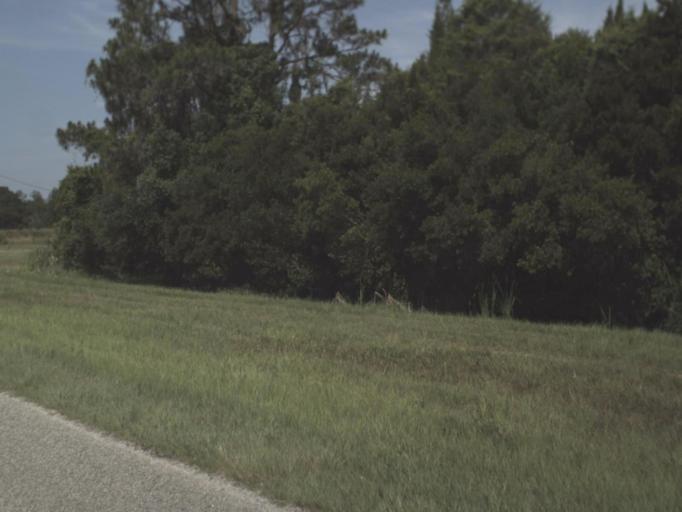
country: US
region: Florida
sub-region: Putnam County
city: East Palatka
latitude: 29.6816
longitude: -81.5771
